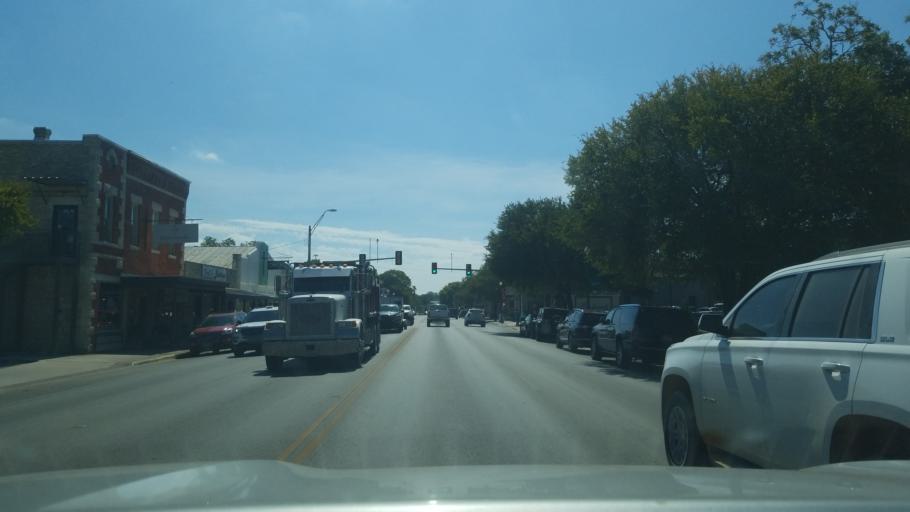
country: US
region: Texas
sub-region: Kendall County
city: Boerne
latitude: 29.7932
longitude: -98.7315
